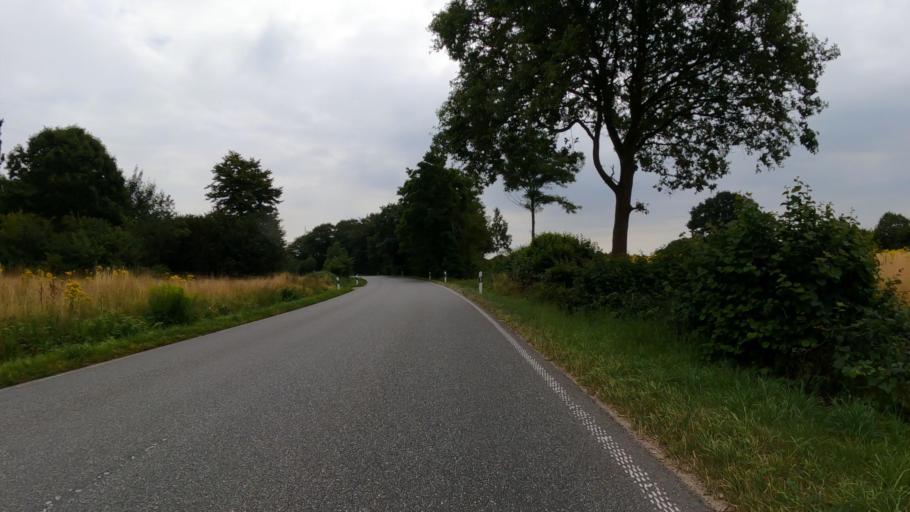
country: DE
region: Schleswig-Holstein
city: Mozen
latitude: 53.9239
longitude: 10.2508
